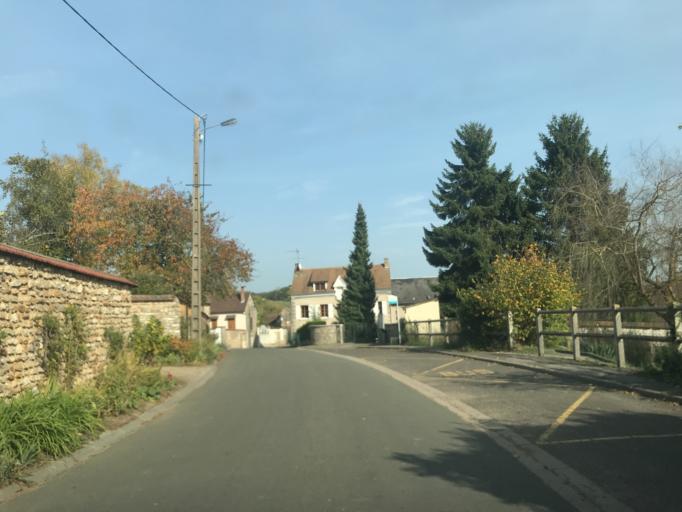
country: FR
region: Haute-Normandie
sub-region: Departement de l'Eure
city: La Chapelle-Reanville
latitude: 49.1100
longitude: 1.3765
